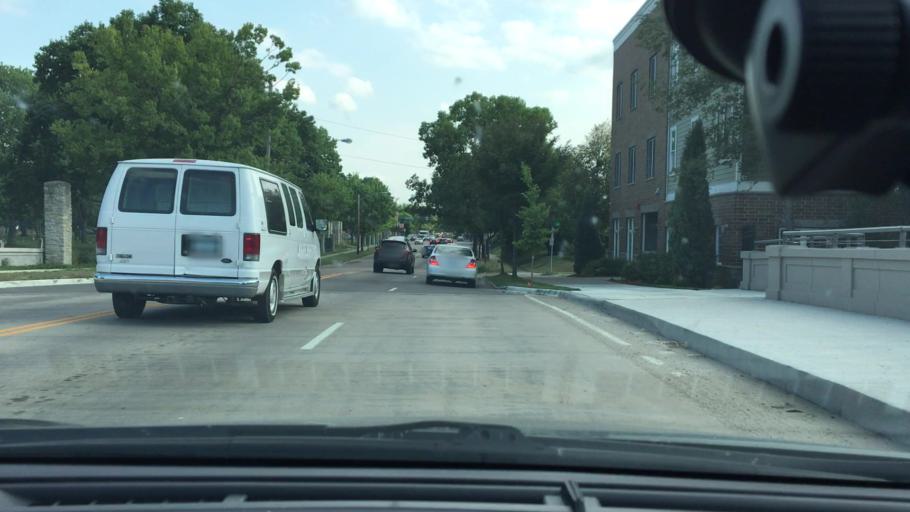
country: US
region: Minnesota
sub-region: Hennepin County
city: Minneapolis
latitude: 44.9505
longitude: -93.2475
